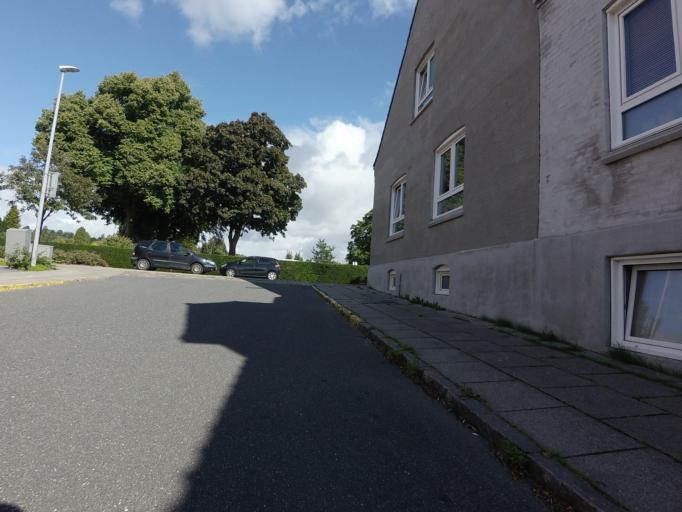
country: DK
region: Central Jutland
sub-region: Silkeborg Kommune
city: Silkeborg
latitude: 56.1649
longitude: 9.5319
